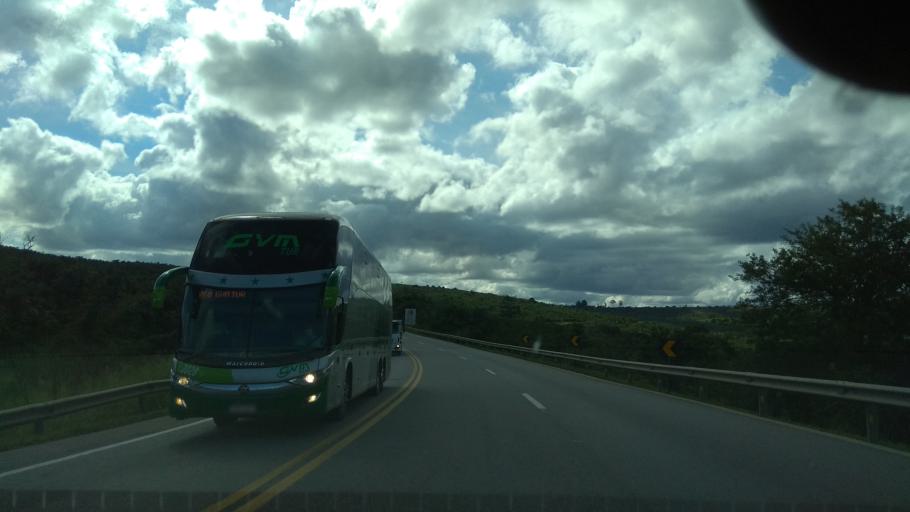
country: BR
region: Bahia
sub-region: Santa Ines
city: Santa Ines
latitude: -13.1263
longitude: -39.9903
